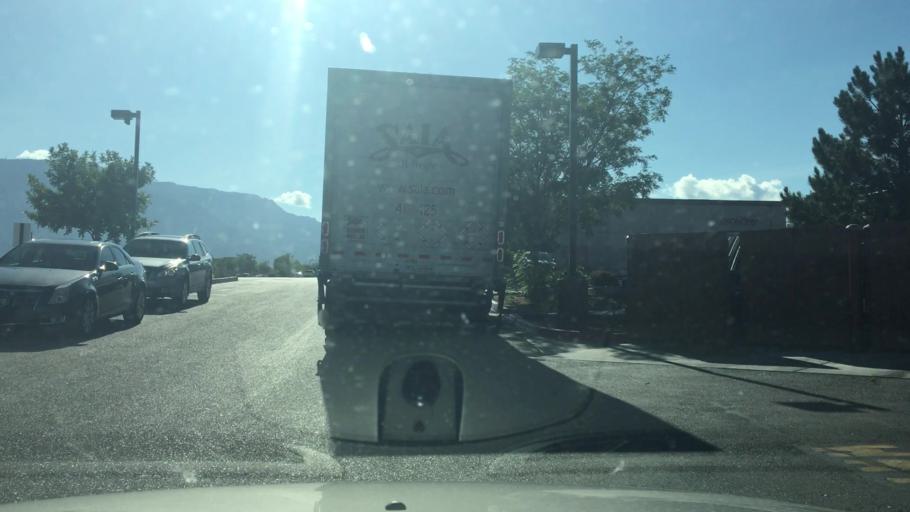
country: US
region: New Mexico
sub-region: Bernalillo County
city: North Valley
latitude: 35.1752
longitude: -106.5683
